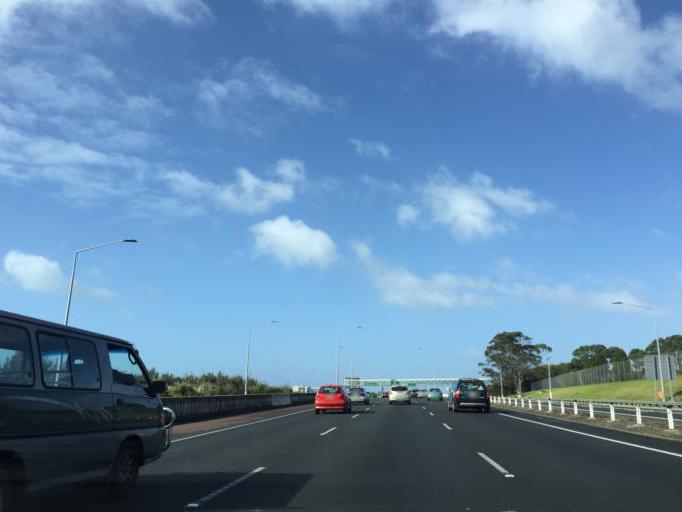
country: NZ
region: Auckland
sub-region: Auckland
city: North Shore
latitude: -36.7948
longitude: 174.7578
